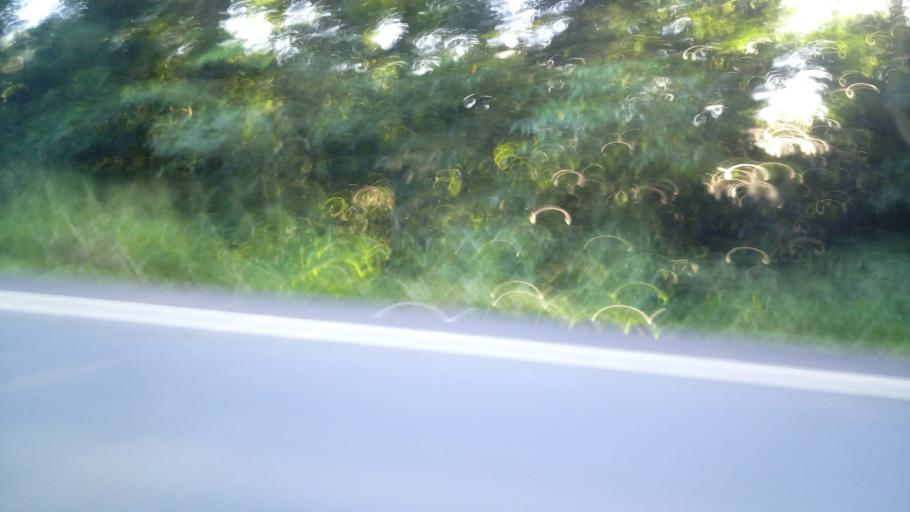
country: AU
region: Queensland
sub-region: Cassowary Coast
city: Innisfail
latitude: -17.6071
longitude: 145.7731
